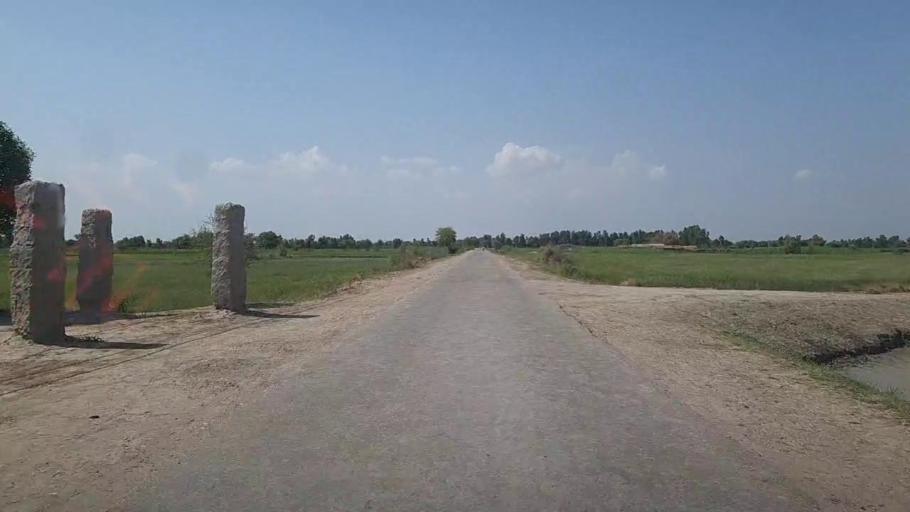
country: PK
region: Sindh
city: Khairpur
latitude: 28.0774
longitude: 69.6381
